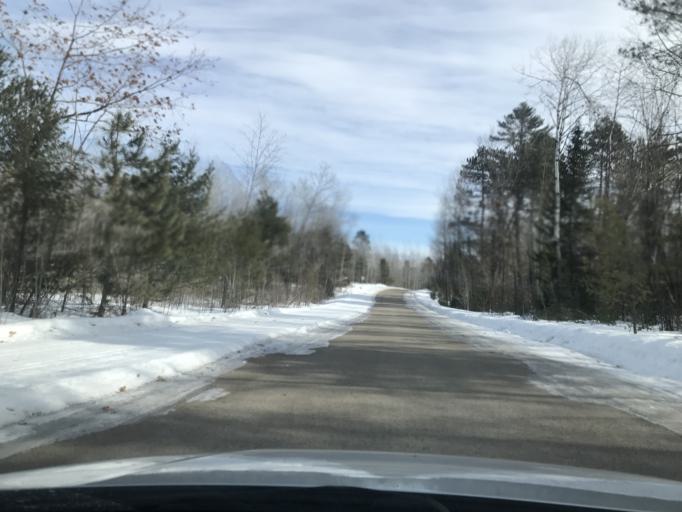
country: US
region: Wisconsin
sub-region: Menominee County
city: Legend Lake
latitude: 45.1094
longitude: -88.4392
